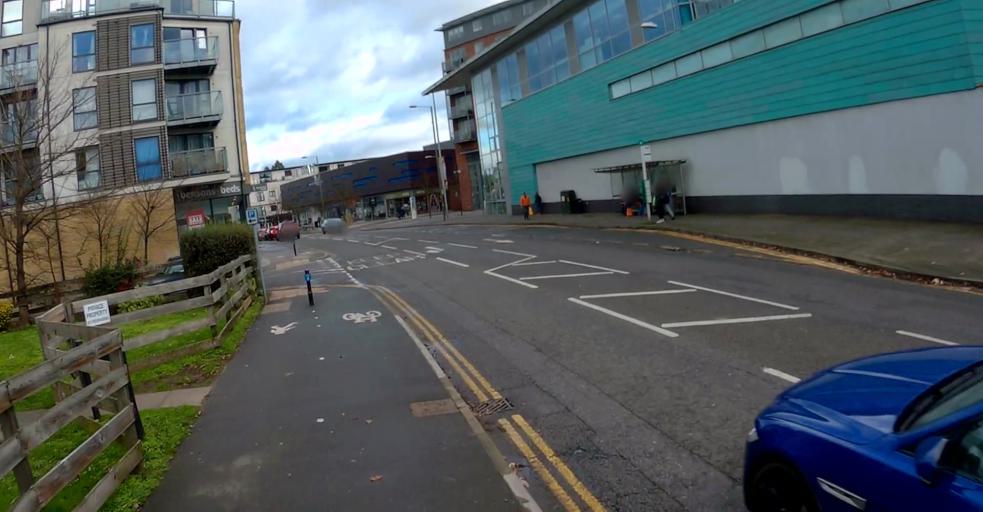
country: GB
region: England
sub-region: Surrey
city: Walton-on-Thames
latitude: 51.3857
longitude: -0.4219
